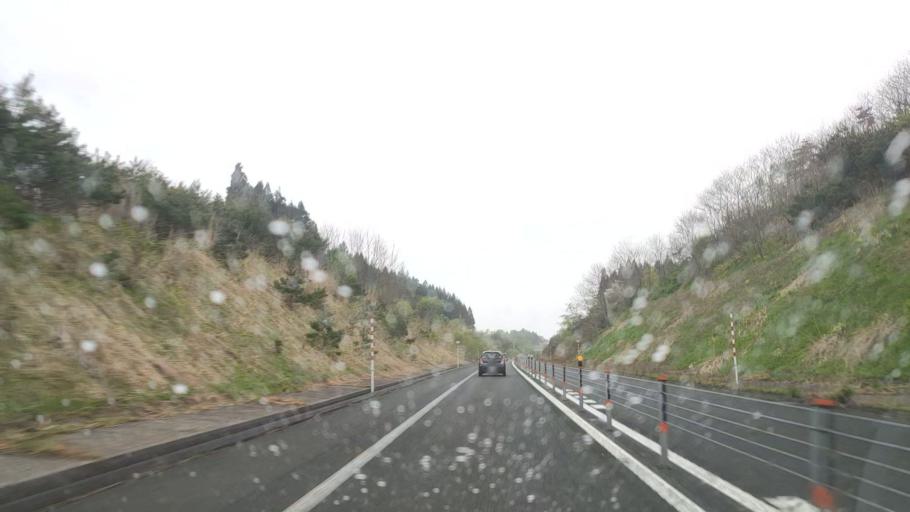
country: JP
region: Akita
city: Noshiromachi
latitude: 40.2044
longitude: 140.1604
